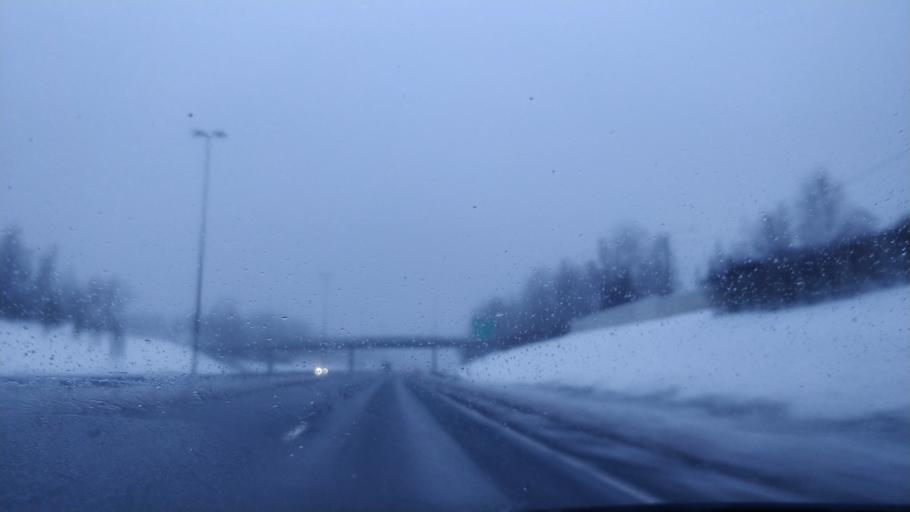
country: FI
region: Lapland
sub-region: Kemi-Tornio
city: Kemi
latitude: 65.7494
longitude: 24.5764
